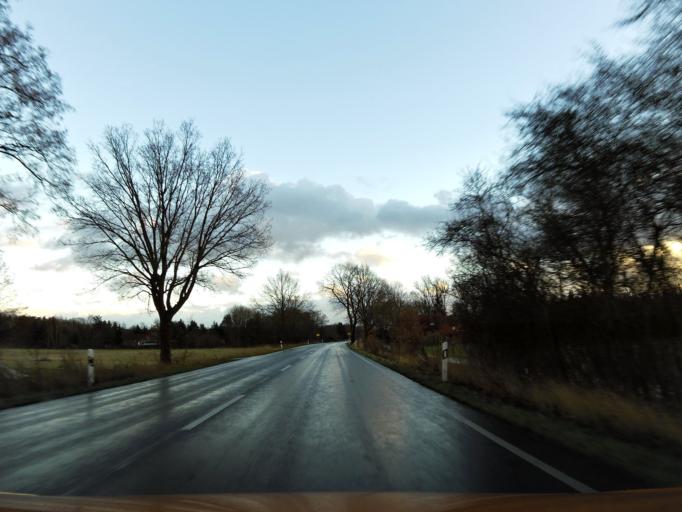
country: DE
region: Lower Saxony
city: Meinersen
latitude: 52.4556
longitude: 10.3048
